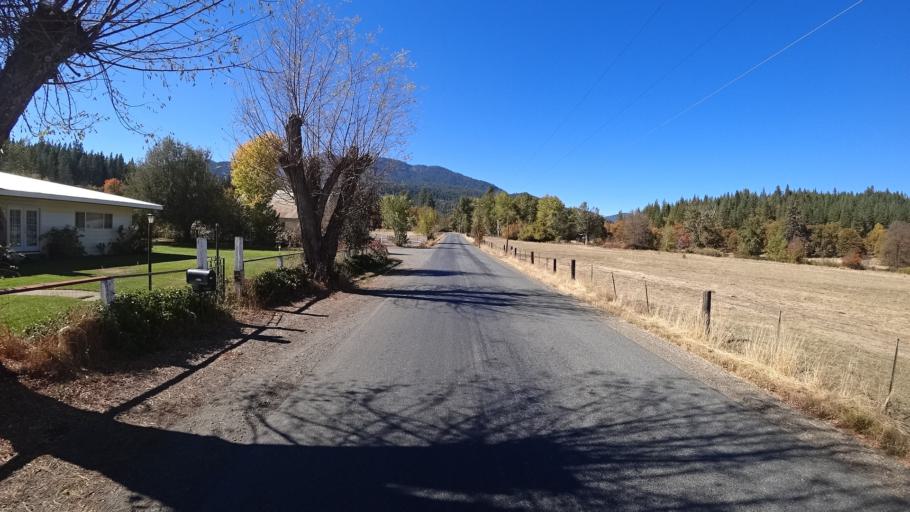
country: US
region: California
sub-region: Siskiyou County
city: Yreka
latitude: 41.6241
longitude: -122.9753
